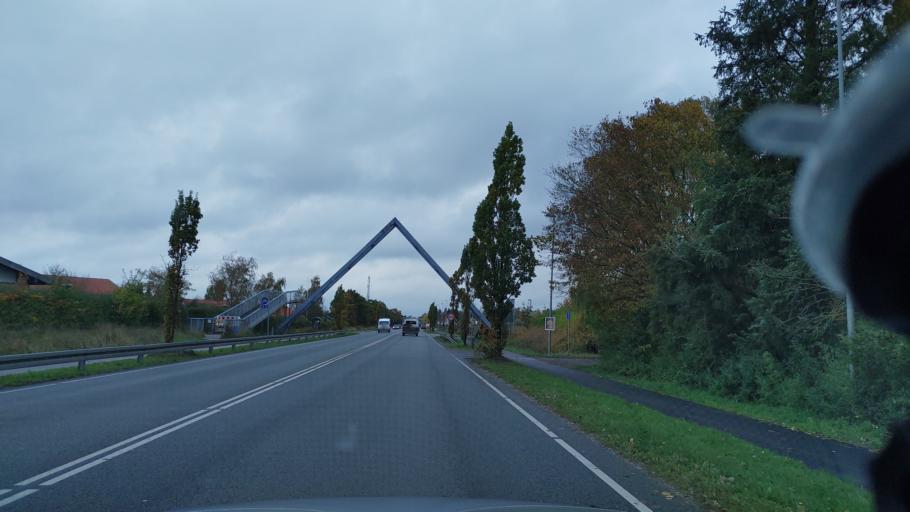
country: DK
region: Zealand
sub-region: Naestved Kommune
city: Naestved
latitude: 55.2423
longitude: 11.7764
